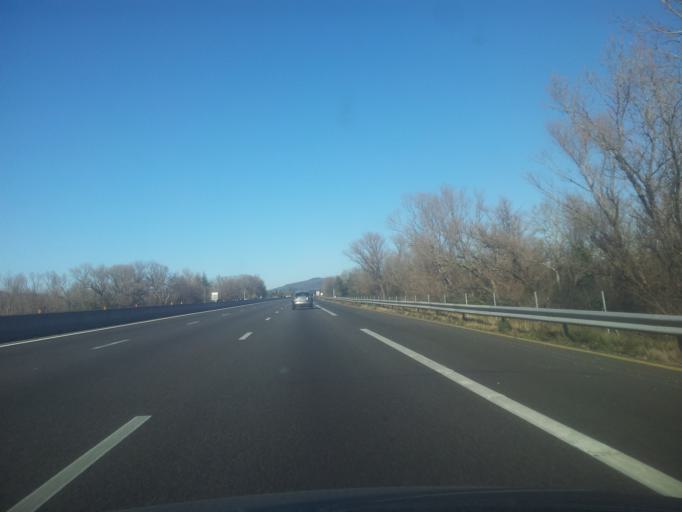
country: FR
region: Rhone-Alpes
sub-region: Departement de la Drome
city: La Garde-Adhemar
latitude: 44.3972
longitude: 4.7295
